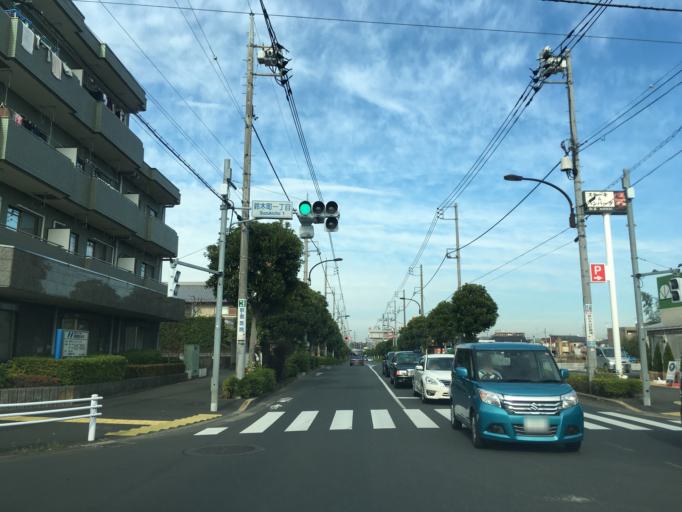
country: JP
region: Tokyo
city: Kokubunji
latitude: 35.7228
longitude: 139.4975
